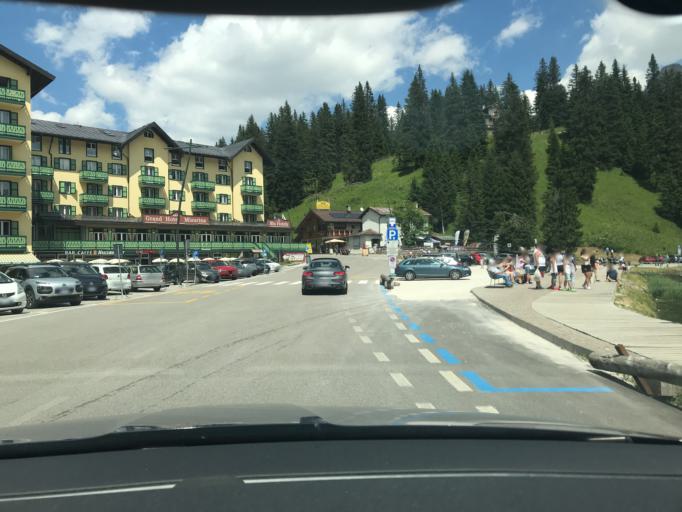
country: IT
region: Veneto
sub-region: Provincia di Belluno
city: Cortina d'Ampezzo
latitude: 46.5837
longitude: 12.2533
